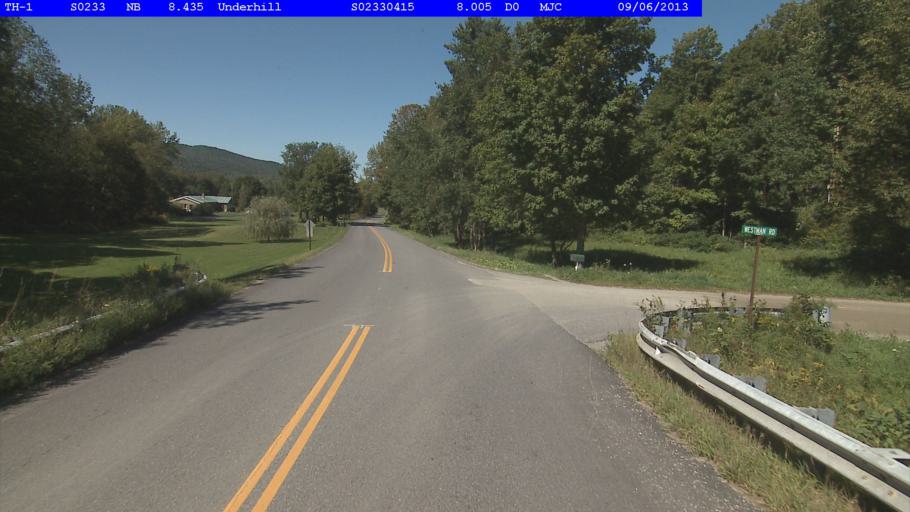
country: US
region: Vermont
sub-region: Chittenden County
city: Jericho
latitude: 44.5800
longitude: -72.8627
